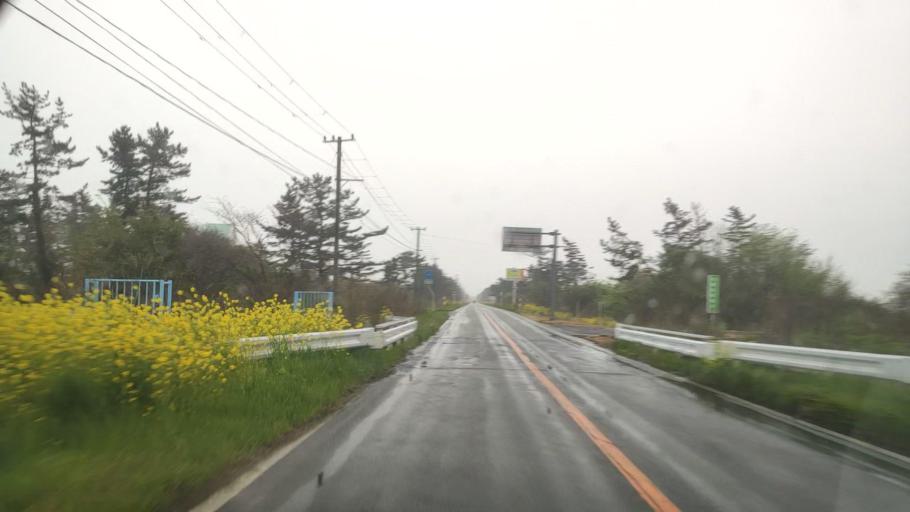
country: JP
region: Akita
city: Tenno
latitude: 40.0316
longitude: 139.9526
